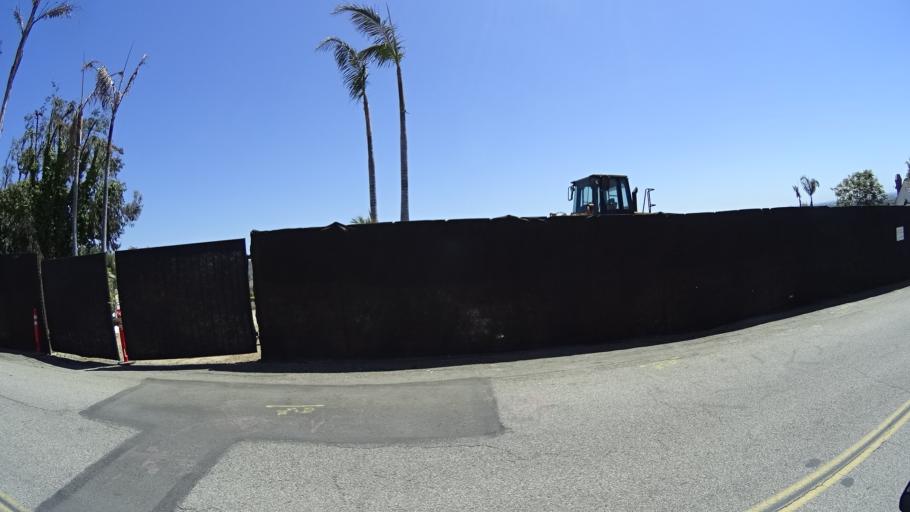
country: US
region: California
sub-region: Orange County
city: Villa Park
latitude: 33.8221
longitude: -117.8041
